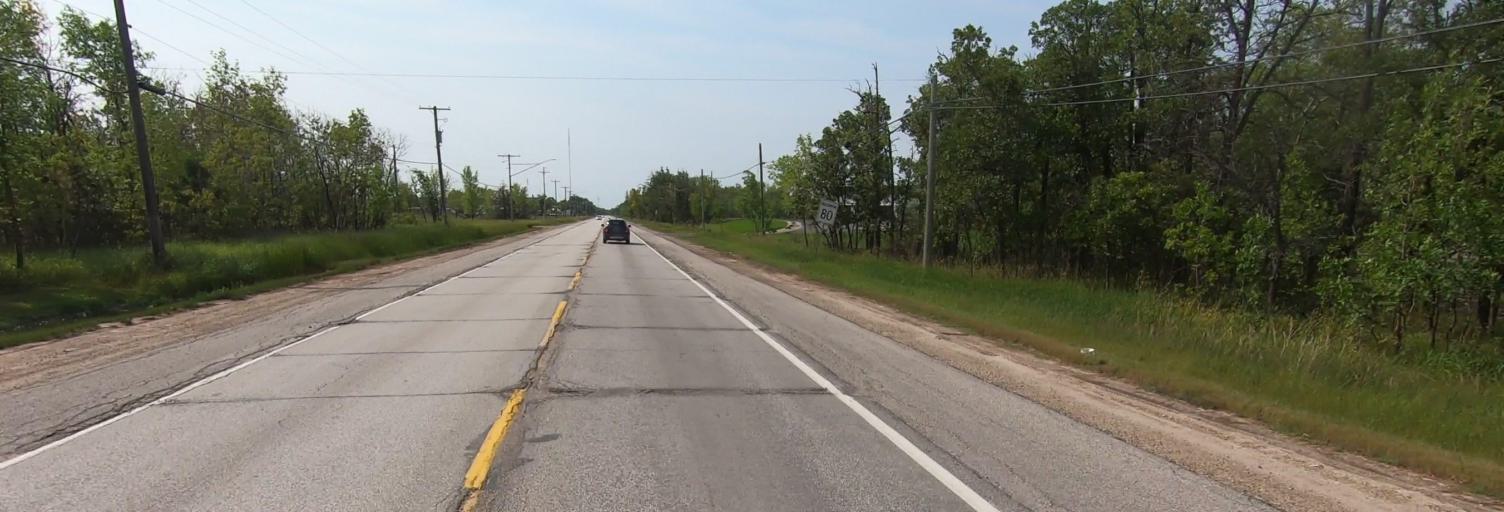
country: CA
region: Manitoba
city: Winnipeg
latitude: 49.7778
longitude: -97.1257
